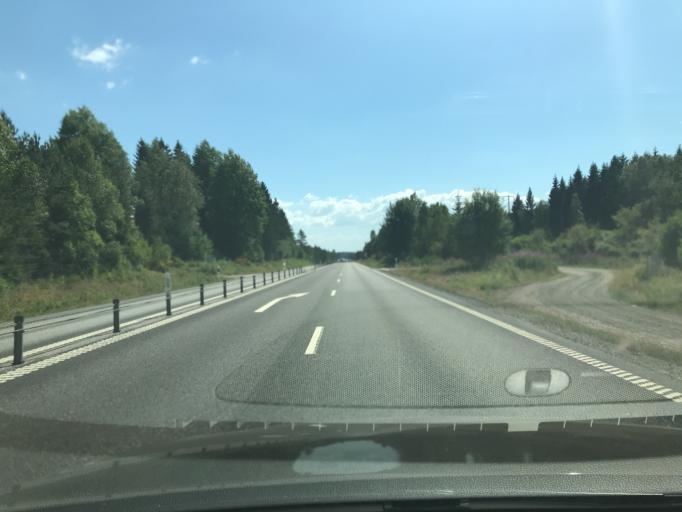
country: SE
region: Kronoberg
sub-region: Almhults Kommun
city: AElmhult
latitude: 56.4911
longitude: 14.1170
